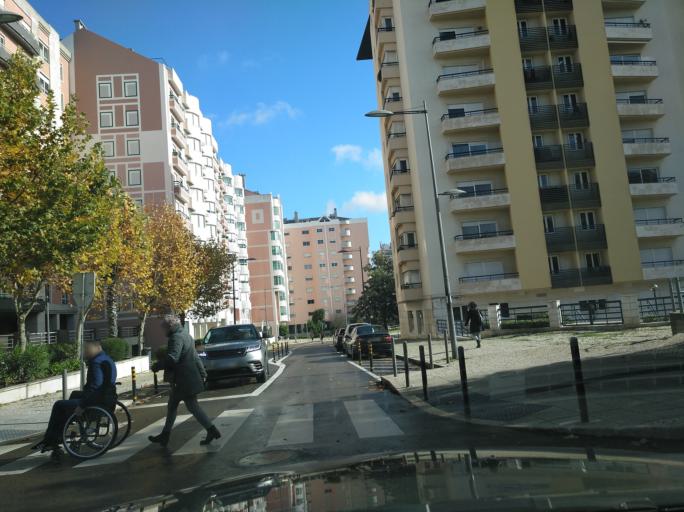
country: PT
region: Lisbon
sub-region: Odivelas
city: Pontinha
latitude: 38.7637
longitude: -9.1771
